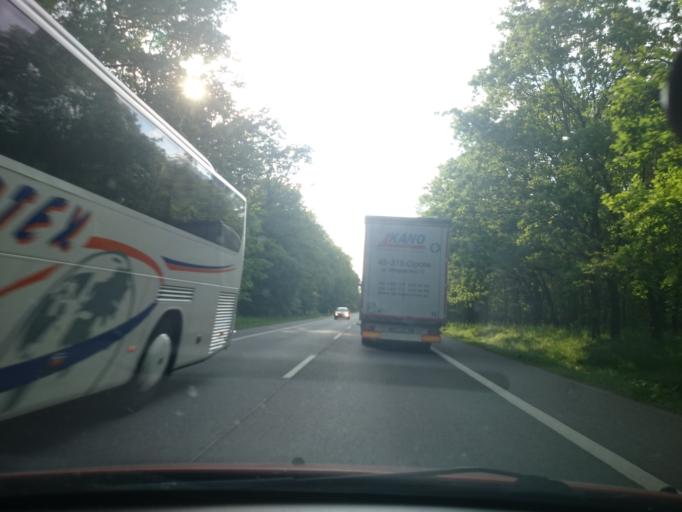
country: PL
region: Opole Voivodeship
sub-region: Powiat opolski
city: Chrzastowice
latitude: 50.6277
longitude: 18.0360
